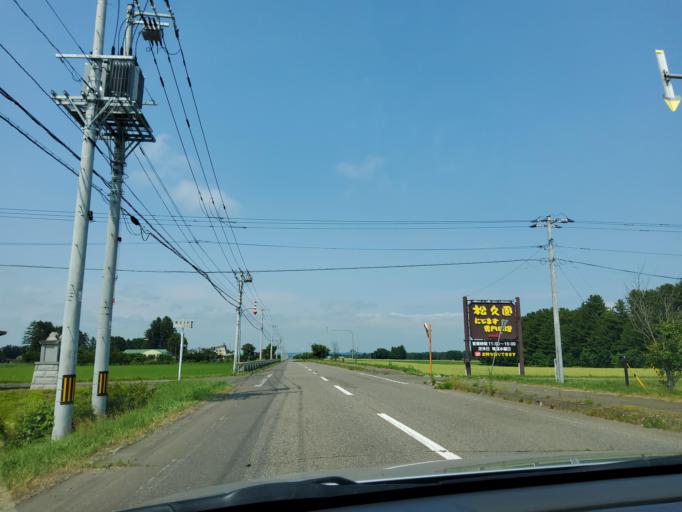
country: JP
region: Hokkaido
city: Obihiro
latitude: 42.8766
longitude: 143.0289
